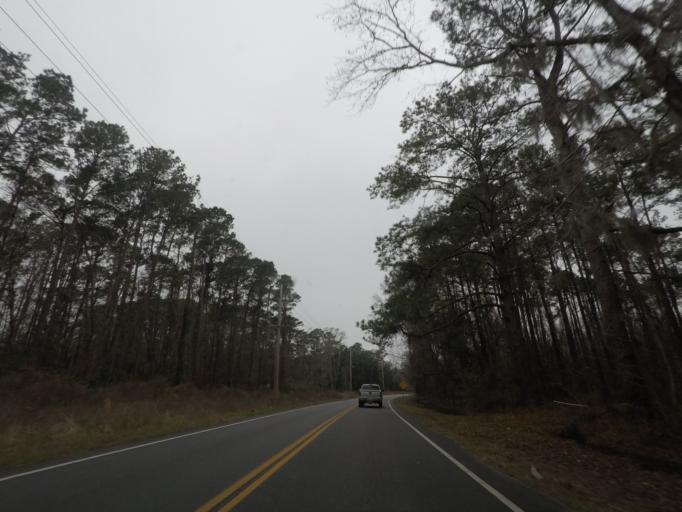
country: US
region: South Carolina
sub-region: Charleston County
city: Meggett
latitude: 32.5820
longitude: -80.3427
